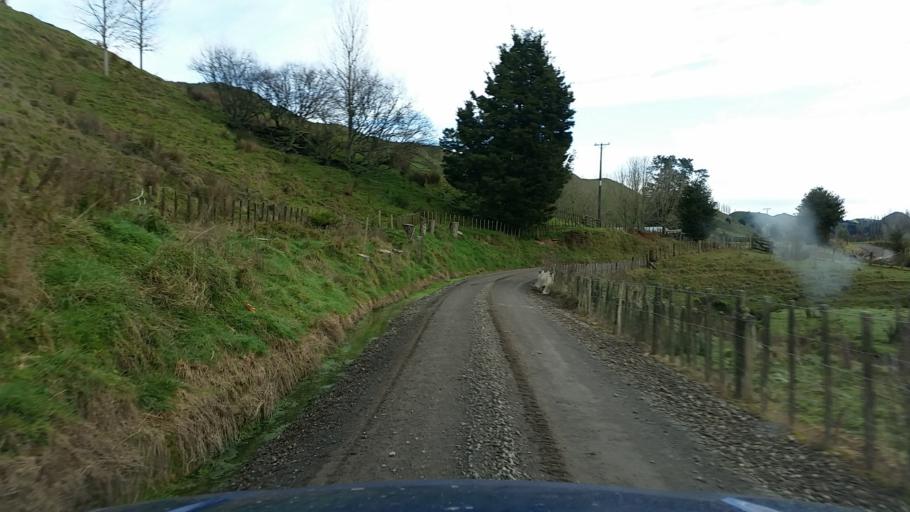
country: NZ
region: Taranaki
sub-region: New Plymouth District
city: Waitara
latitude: -39.0906
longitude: 174.8367
